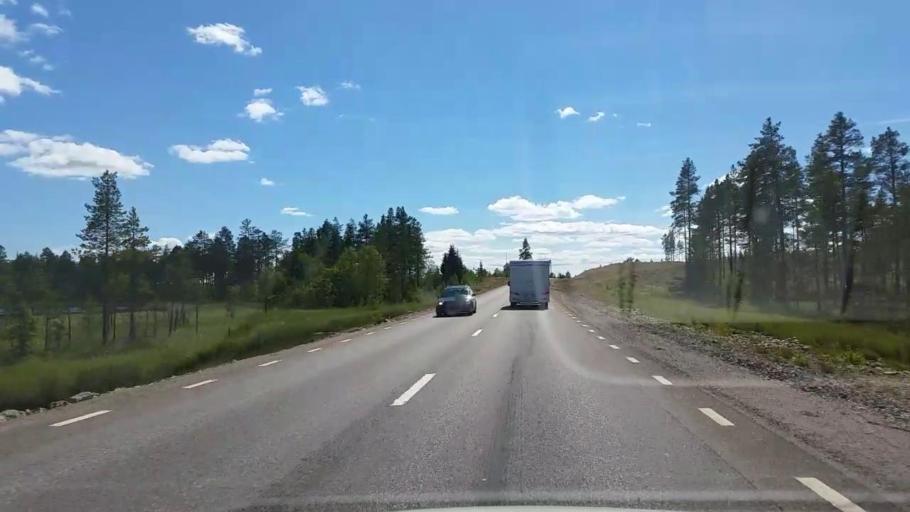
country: SE
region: Gaevleborg
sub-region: Bollnas Kommun
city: Vittsjo
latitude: 61.1044
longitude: 15.8572
